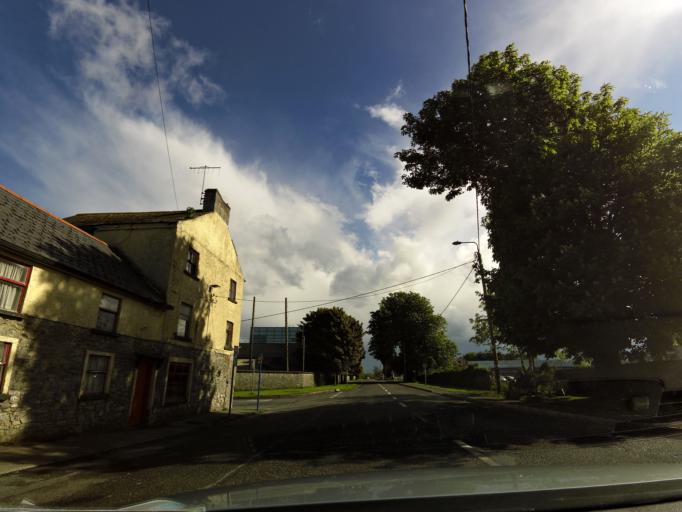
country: IE
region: Munster
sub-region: North Tipperary
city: Templemore
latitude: 52.7928
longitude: -7.8439
